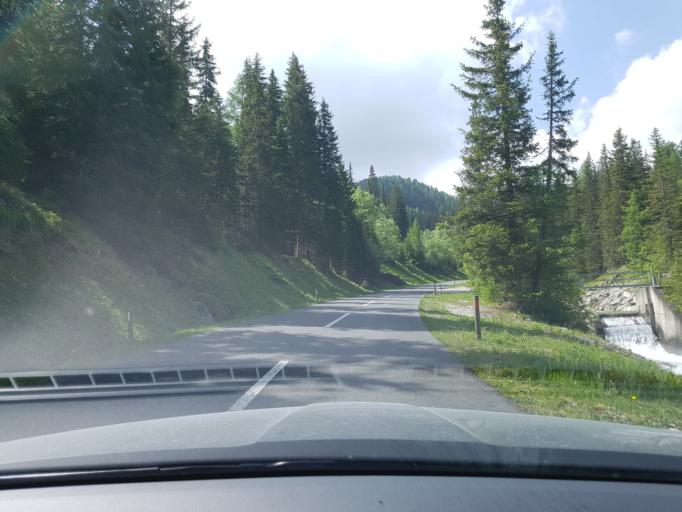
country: AT
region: Salzburg
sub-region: Politischer Bezirk Tamsweg
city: Thomatal
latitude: 46.9590
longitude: 13.7296
